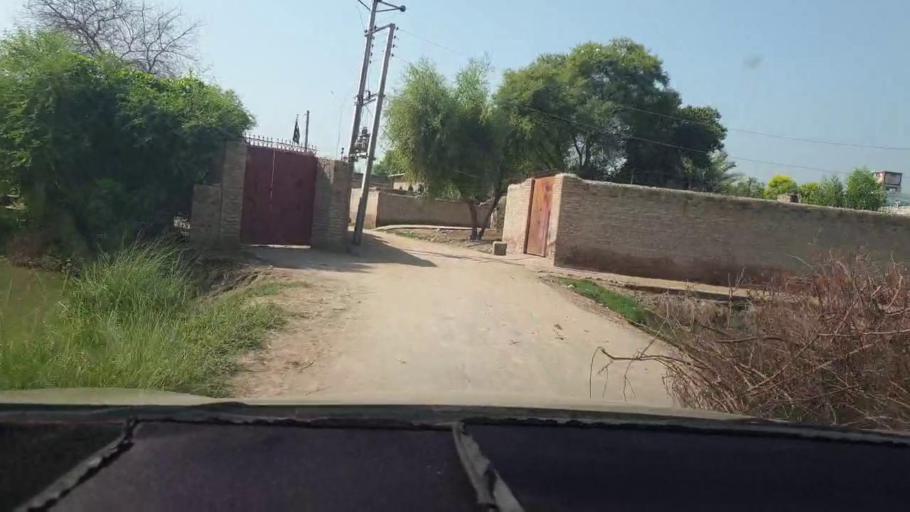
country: PK
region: Sindh
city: Kambar
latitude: 27.5728
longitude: 68.0743
